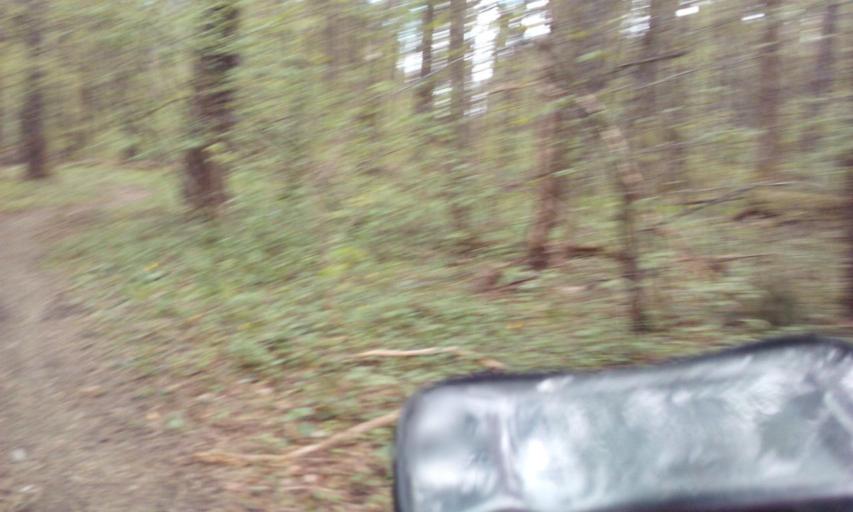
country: RU
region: Moskovskaya
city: Gorki Vtoryye
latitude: 55.6722
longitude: 37.1627
